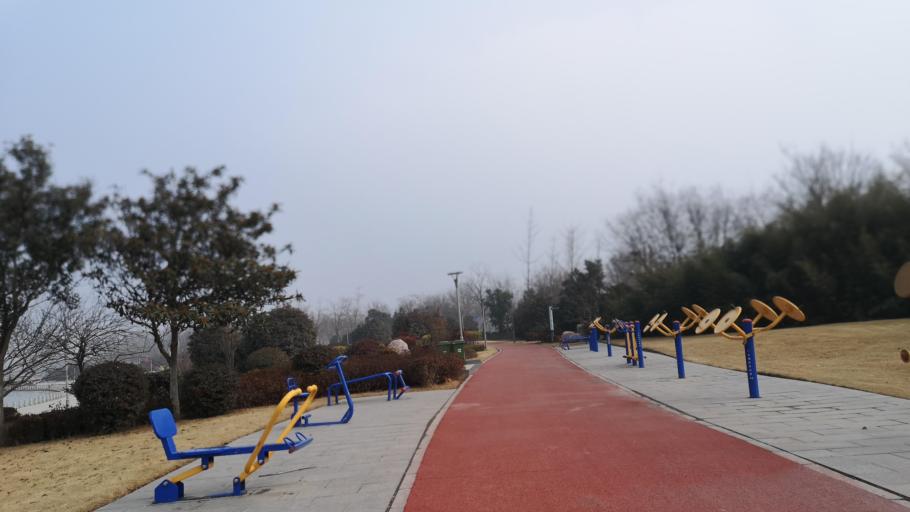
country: CN
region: Henan Sheng
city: Zhongyuanlu
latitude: 35.8010
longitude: 115.0573
